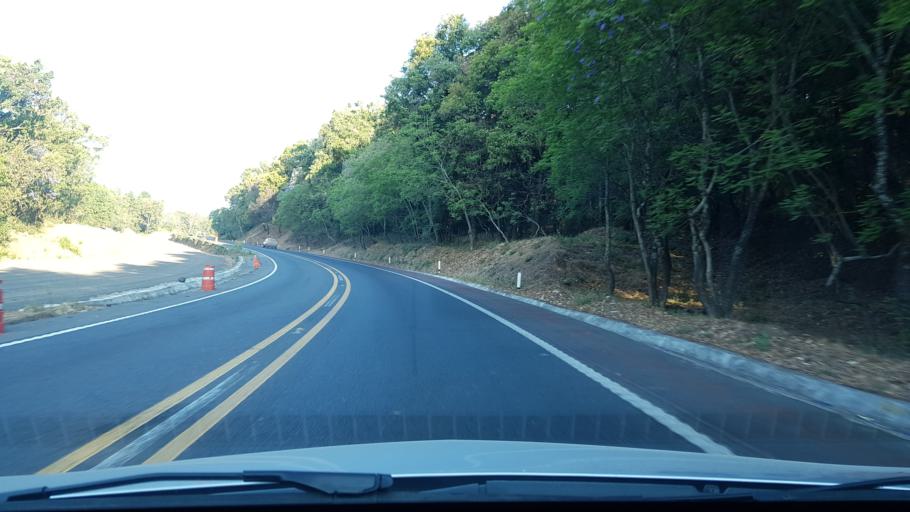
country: MX
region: Morelos
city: Tepoztlan
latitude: 19.0036
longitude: -99.1264
